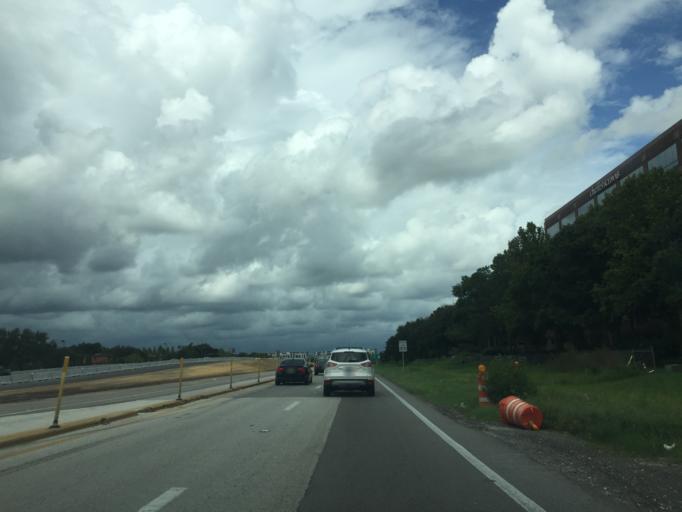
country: US
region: Florida
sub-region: Orange County
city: Eatonville
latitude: 28.6363
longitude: -81.4028
